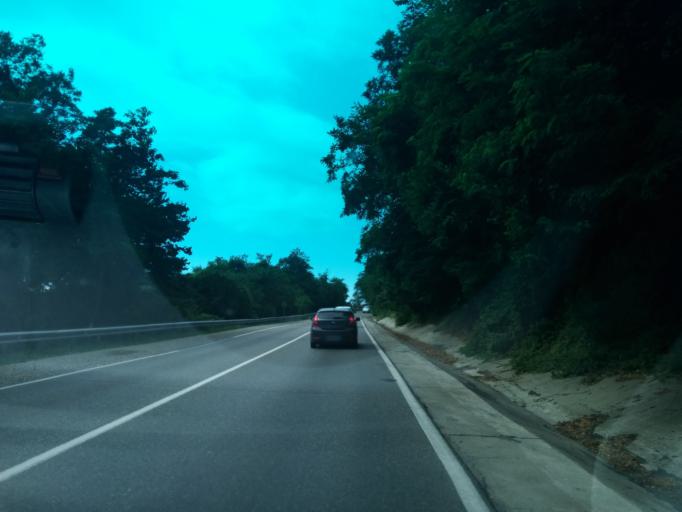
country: RU
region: Krasnodarskiy
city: Nebug
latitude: 44.1754
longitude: 38.9734
